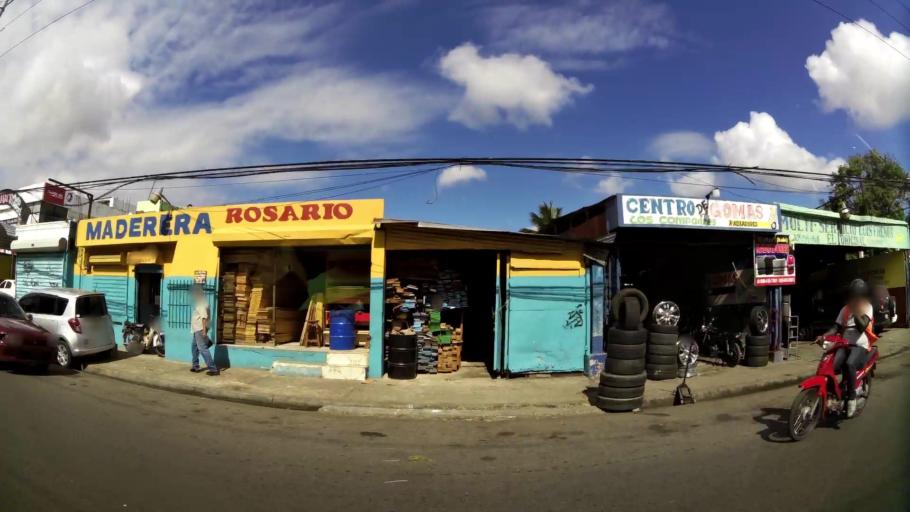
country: DO
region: Santo Domingo
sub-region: Santo Domingo
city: Santo Domingo Este
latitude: 18.5021
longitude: -69.8604
